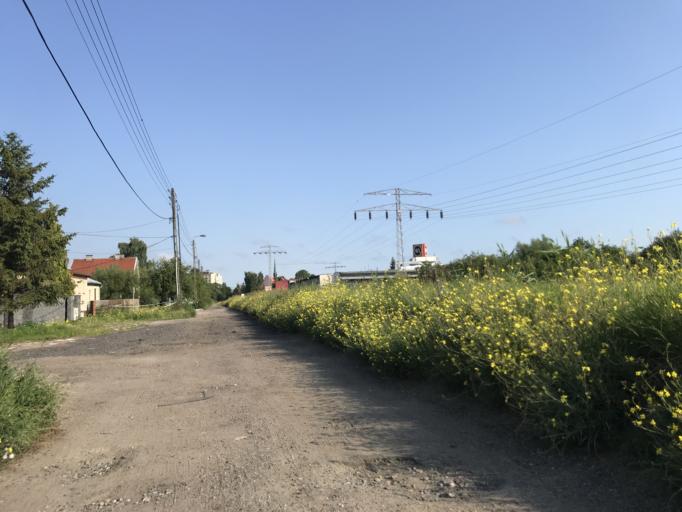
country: PL
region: Pomeranian Voivodeship
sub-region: Gdansk
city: Gdansk
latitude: 54.3460
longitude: 18.6795
